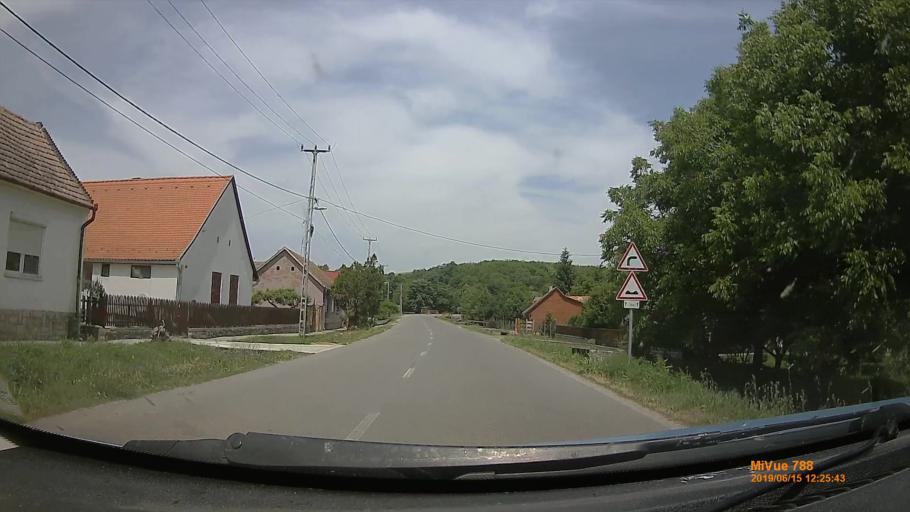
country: HU
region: Baranya
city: Buekkoesd
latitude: 46.1169
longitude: 17.9961
